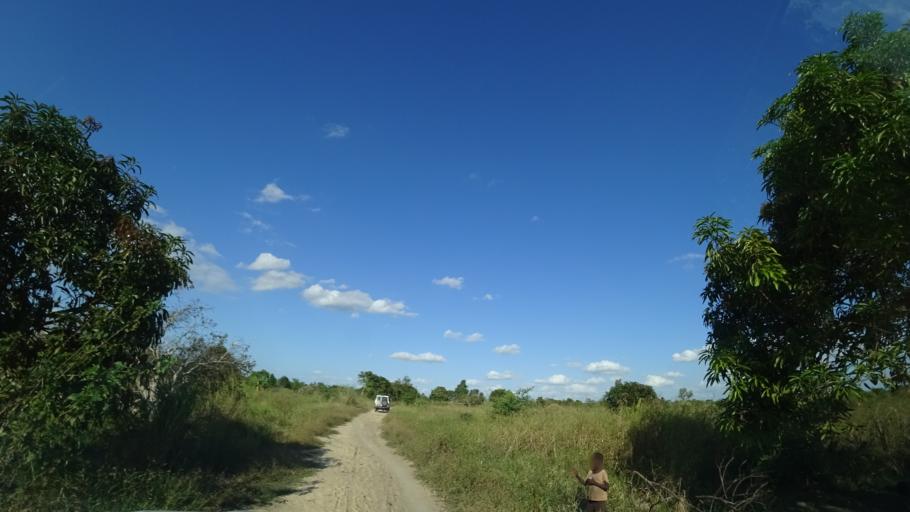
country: MZ
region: Sofala
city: Dondo
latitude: -19.3509
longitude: 34.5865
